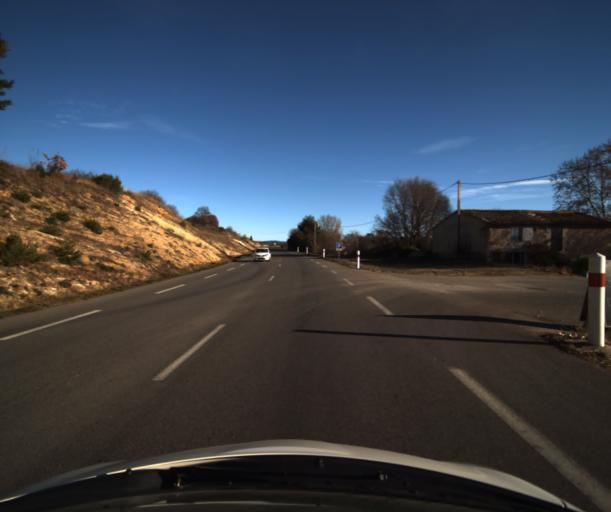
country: FR
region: Provence-Alpes-Cote d'Azur
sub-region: Departement du Vaucluse
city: Pertuis
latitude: 43.7086
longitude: 5.5195
